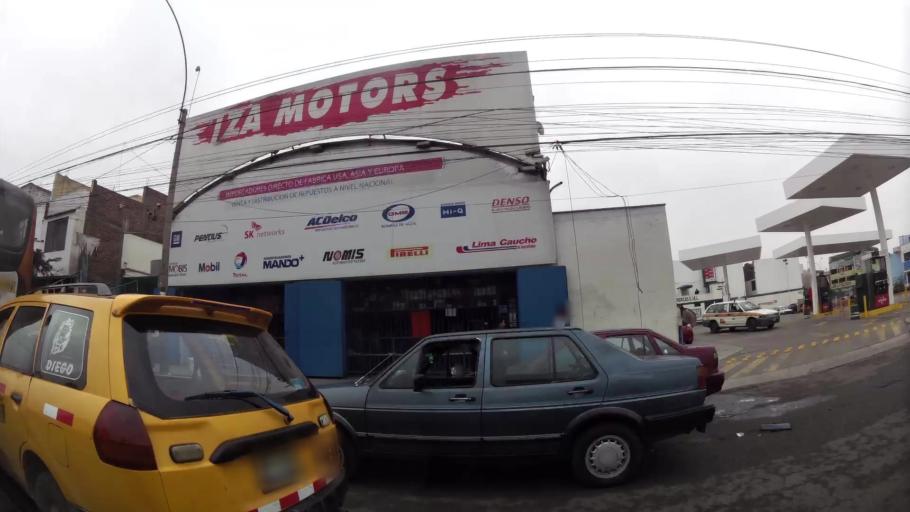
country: PE
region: Lima
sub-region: Lima
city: San Luis
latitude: -12.0755
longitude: -77.0166
